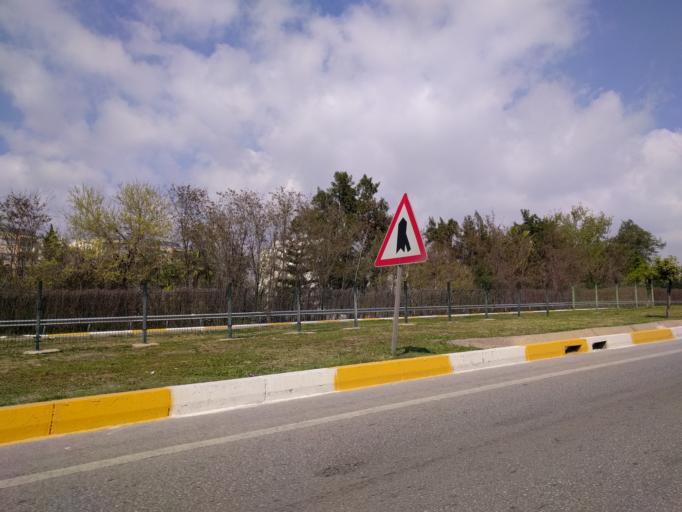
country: TR
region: Antalya
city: Antalya
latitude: 36.9009
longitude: 30.6634
